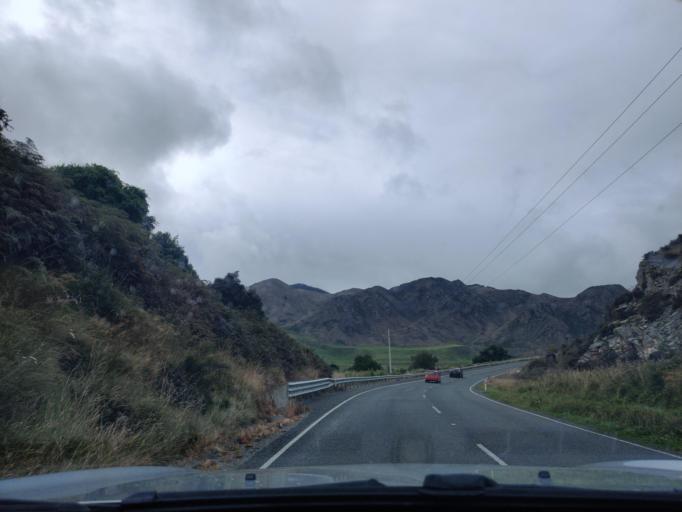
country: NZ
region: Canterbury
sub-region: Hurunui District
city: Amberley
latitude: -42.6286
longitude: 172.7701
